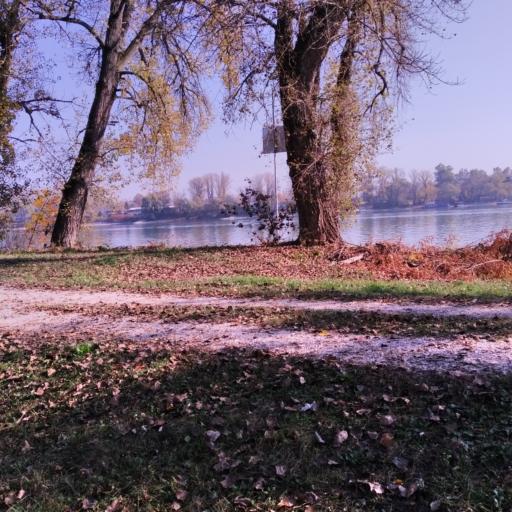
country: HU
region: Budapest
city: Budapest IV. keruelet
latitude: 47.5914
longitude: 19.0733
